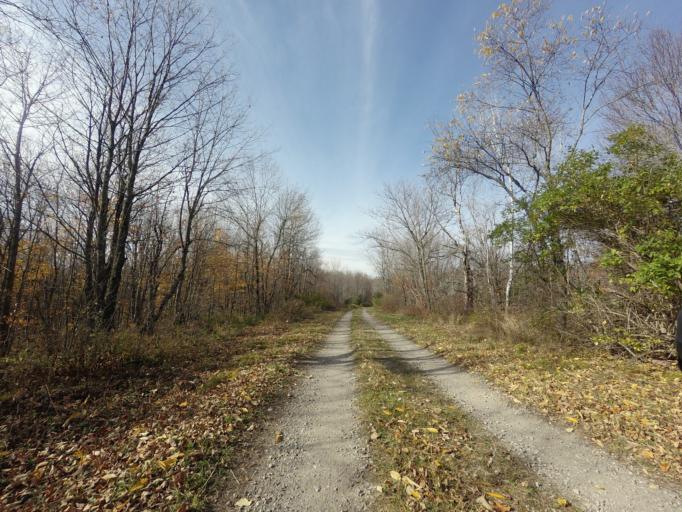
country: CA
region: Quebec
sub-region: Outaouais
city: Wakefield
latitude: 45.5193
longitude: -75.9145
